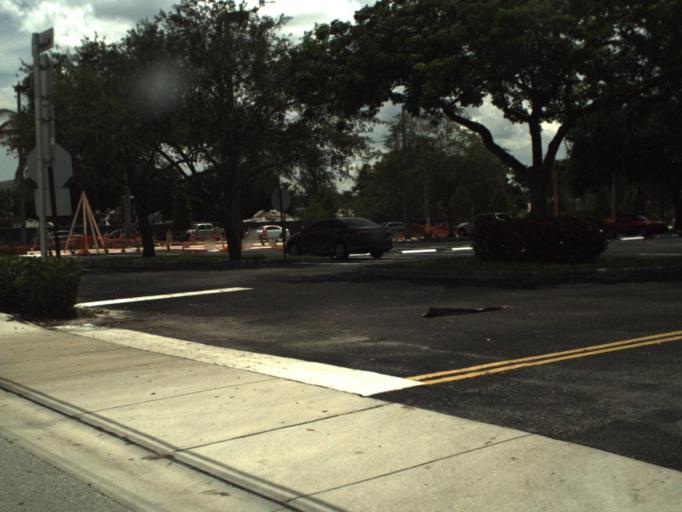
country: US
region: Florida
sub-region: Broward County
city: Coral Springs
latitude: 26.2701
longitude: -80.2503
